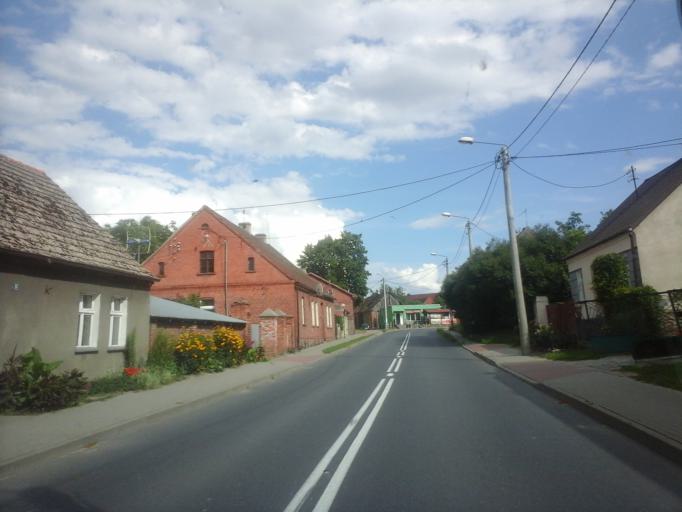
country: PL
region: West Pomeranian Voivodeship
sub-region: Powiat stargardzki
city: Suchan
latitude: 53.2275
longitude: 15.2995
